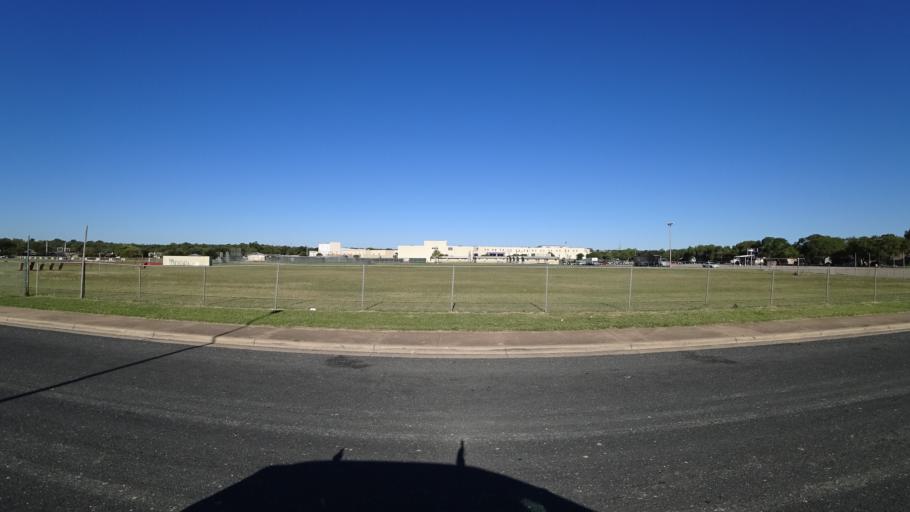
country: US
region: Texas
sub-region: Travis County
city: Hornsby Bend
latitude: 30.3117
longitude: -97.6537
